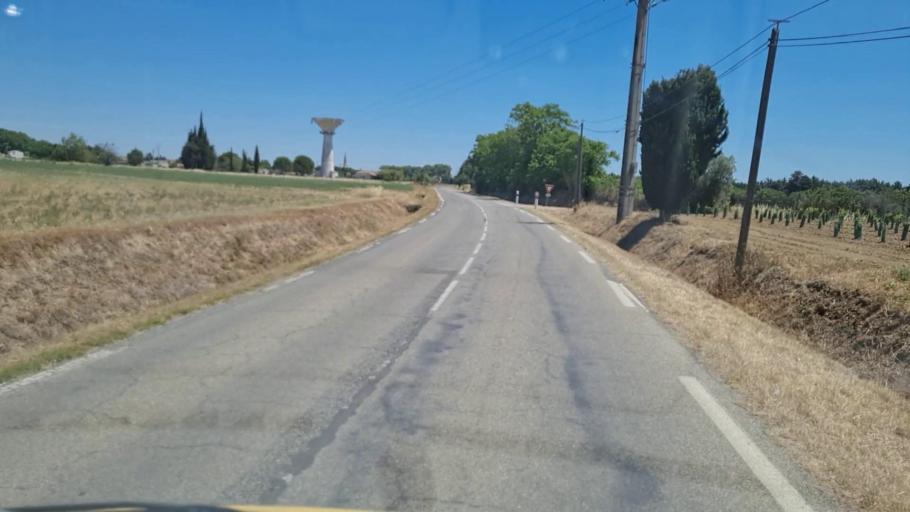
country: FR
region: Languedoc-Roussillon
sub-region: Departement du Gard
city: Aimargues
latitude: 43.6887
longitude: 4.1952
